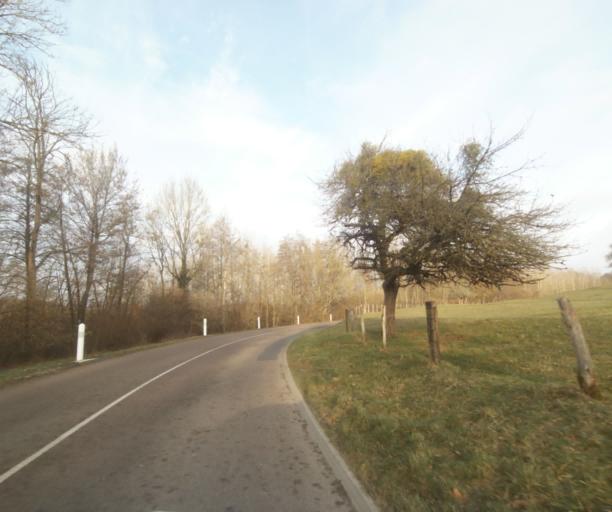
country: FR
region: Champagne-Ardenne
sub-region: Departement de la Marne
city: Sermaize-les-Bains
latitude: 48.7421
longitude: 4.9063
